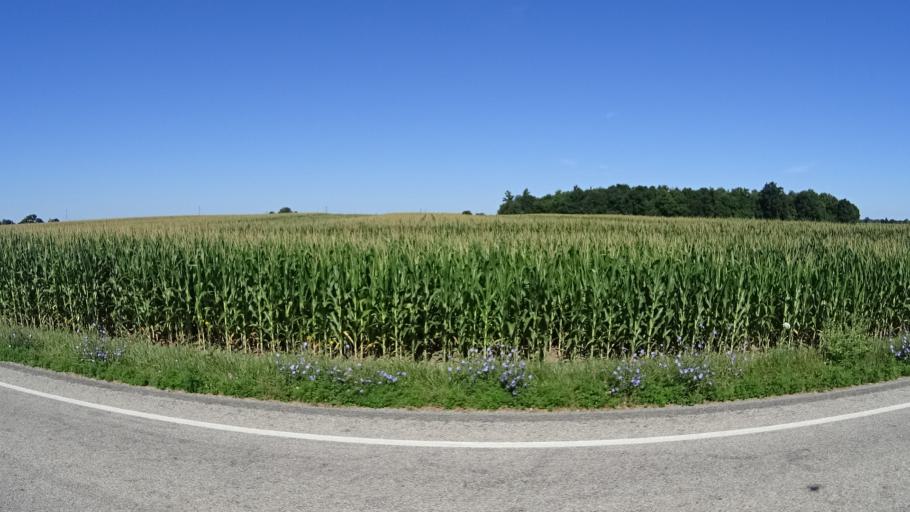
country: US
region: Ohio
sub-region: Erie County
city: Sandusky
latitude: 41.3855
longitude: -82.7223
